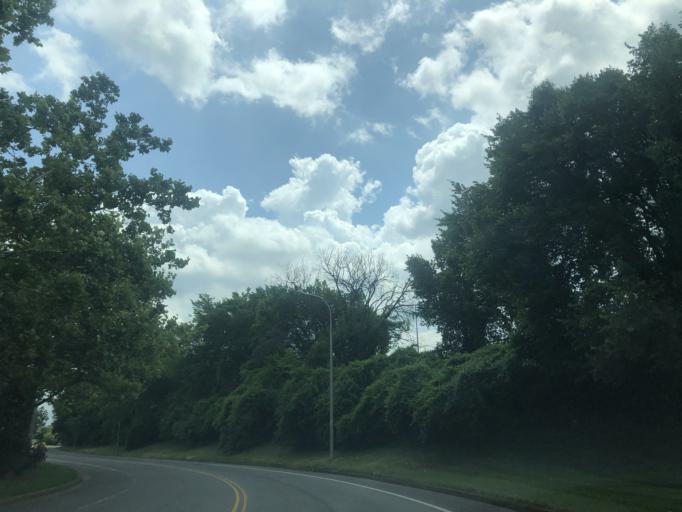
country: US
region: Tennessee
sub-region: Davidson County
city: Nashville
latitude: 36.1916
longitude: -86.7895
